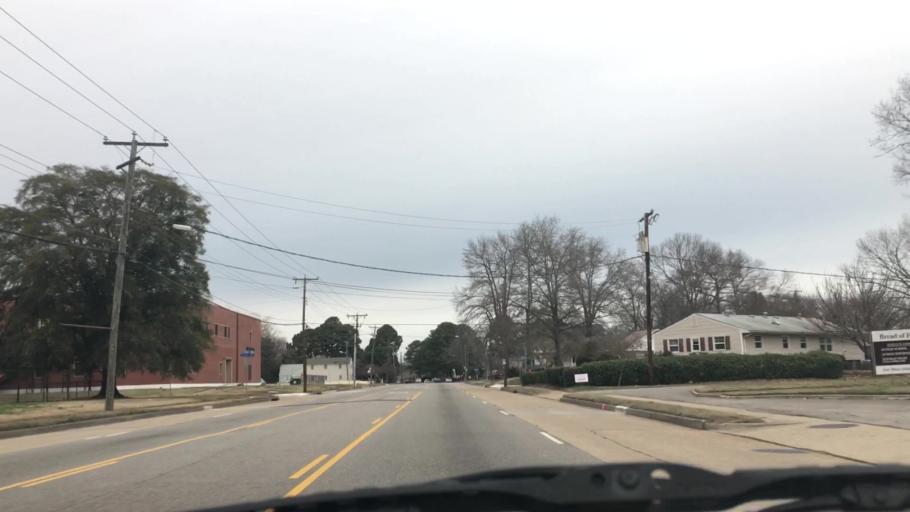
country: US
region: Virginia
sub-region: City of Norfolk
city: Norfolk
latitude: 36.8798
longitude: -76.2335
